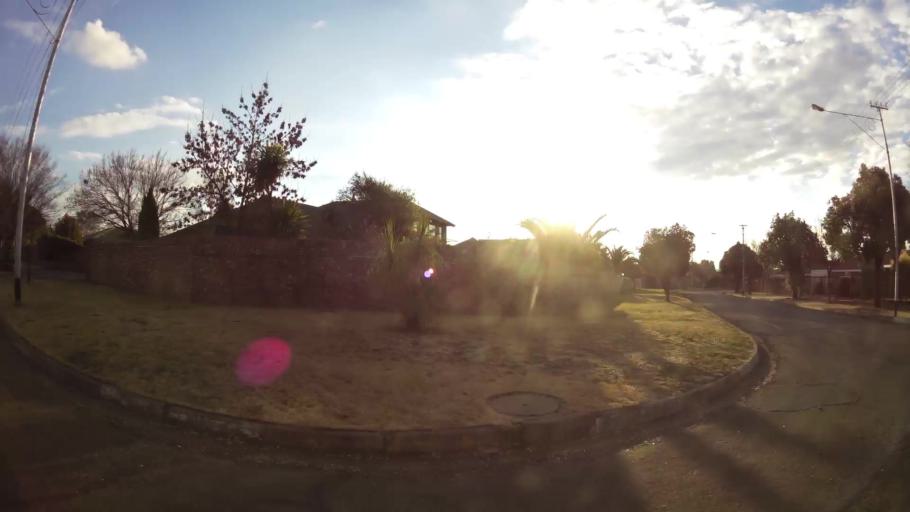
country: ZA
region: Orange Free State
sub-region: Mangaung Metropolitan Municipality
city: Bloemfontein
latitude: -29.1378
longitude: 26.1966
